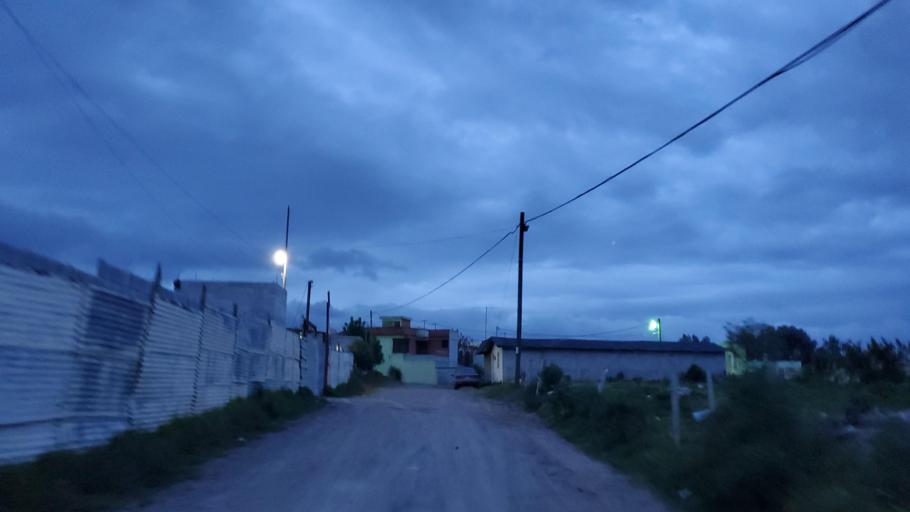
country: GT
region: Quetzaltenango
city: Quetzaltenango
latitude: 14.8295
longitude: -91.5396
